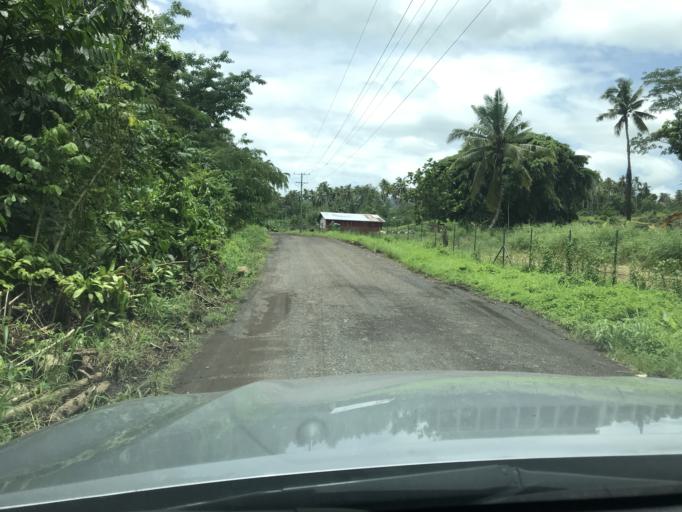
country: WS
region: Tuamasaga
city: Afenga
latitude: -13.8206
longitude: -171.8838
